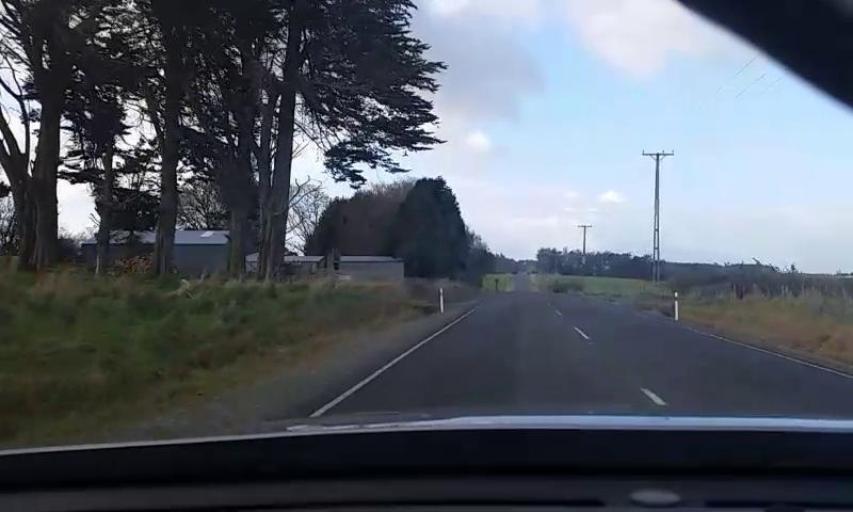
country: NZ
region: Southland
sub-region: Invercargill City
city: Invercargill
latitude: -46.3807
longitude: 168.4213
